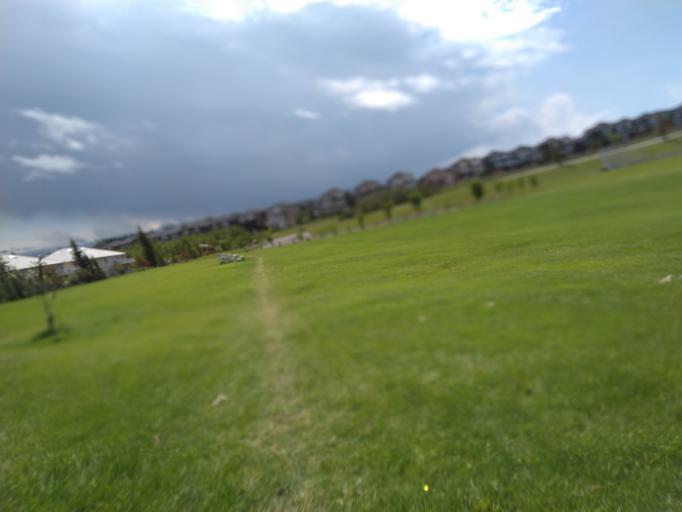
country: CA
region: Alberta
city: Cochrane
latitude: 51.1857
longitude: -114.5056
